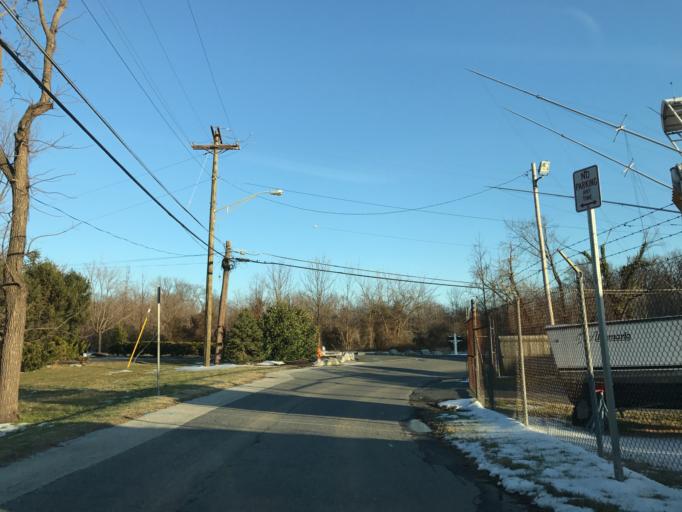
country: US
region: Maryland
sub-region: Baltimore County
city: Bowleys Quarters
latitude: 39.2849
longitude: -76.3947
